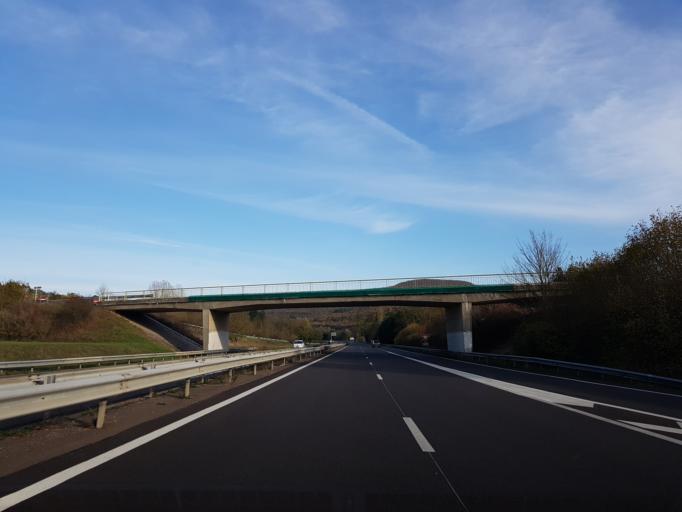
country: FR
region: Bourgogne
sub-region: Departement de la Cote-d'Or
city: Fleurey-sur-Ouche
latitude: 47.2981
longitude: 4.8030
